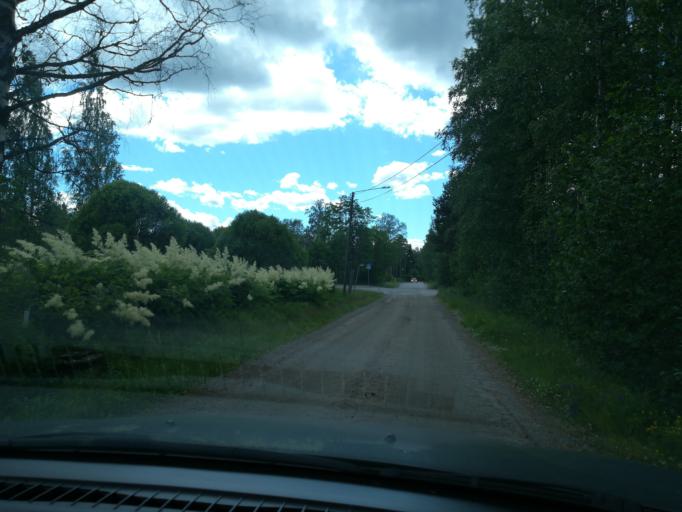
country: FI
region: Southern Savonia
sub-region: Mikkeli
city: Hirvensalmi
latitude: 61.6491
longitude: 26.7754
